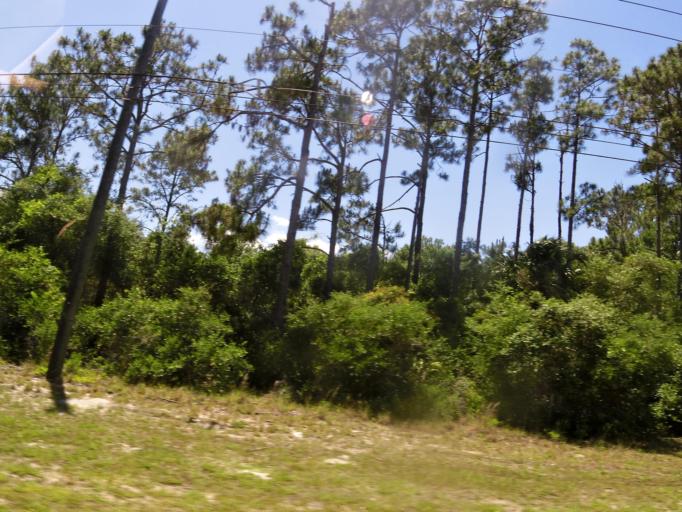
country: US
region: Florida
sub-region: Flagler County
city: Flagler Beach
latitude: 29.4499
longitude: -81.1644
